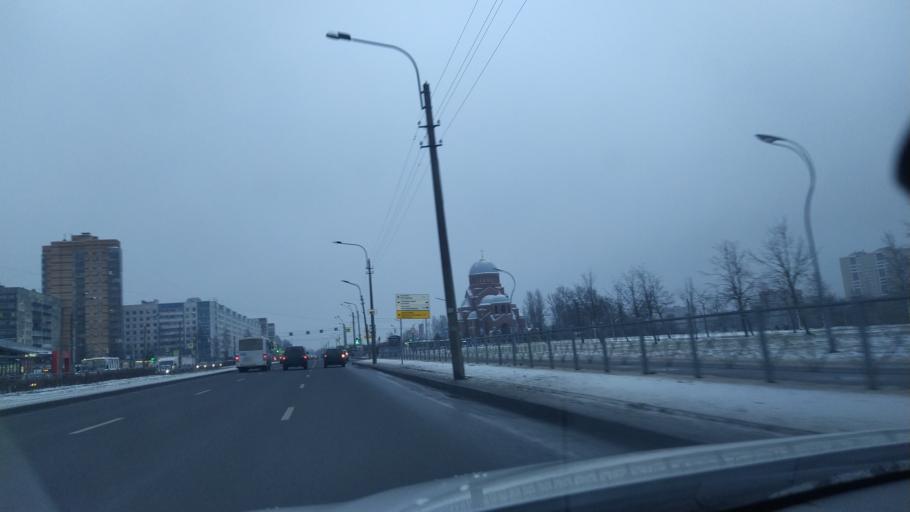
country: RU
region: St.-Petersburg
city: Grazhdanka
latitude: 60.0264
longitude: 30.4075
